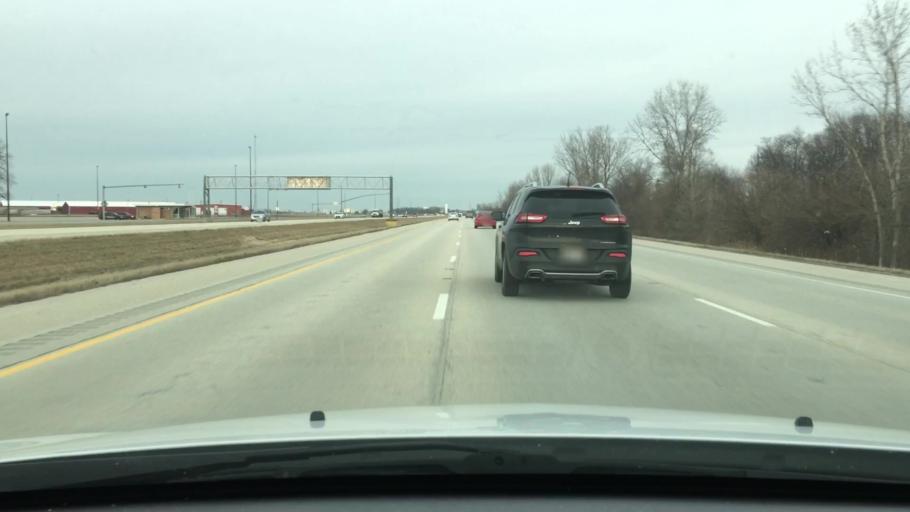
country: US
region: Illinois
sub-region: Sangamon County
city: Williamsville
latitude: 39.9279
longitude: -89.5729
